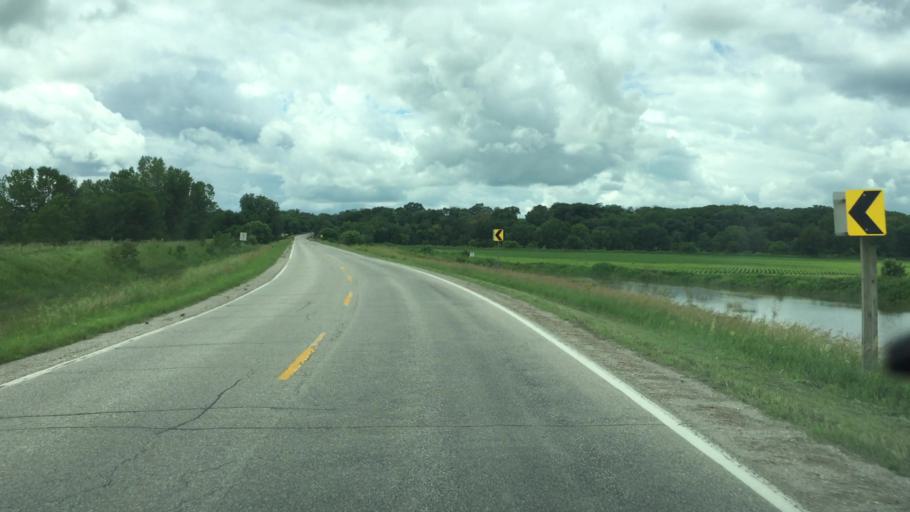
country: US
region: Iowa
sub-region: Jasper County
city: Monroe
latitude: 41.5768
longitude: -93.0324
